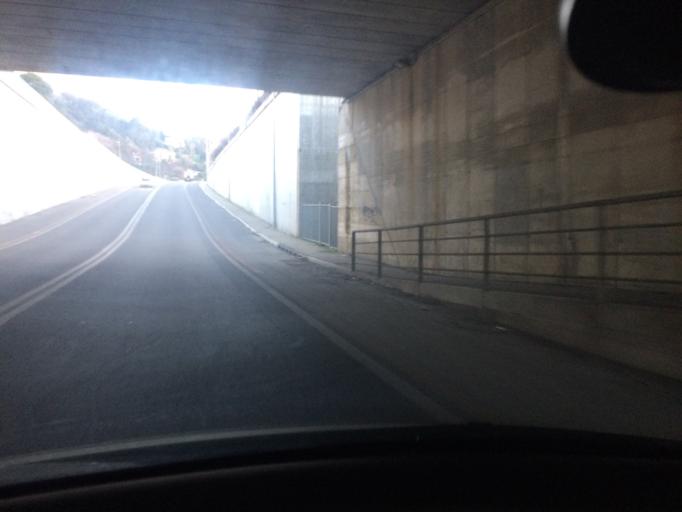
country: IT
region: Tuscany
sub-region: Provincia di Massa-Carrara
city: Massa
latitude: 44.0345
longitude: 10.0993
